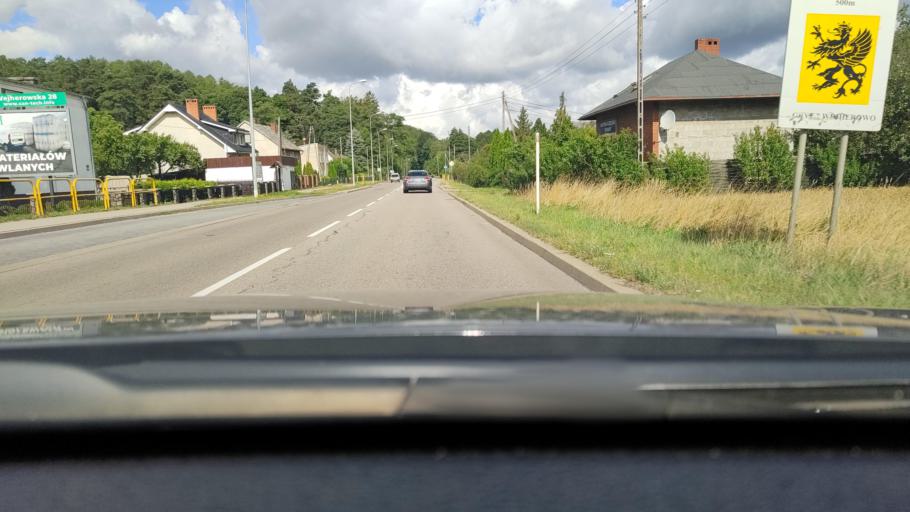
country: PL
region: Pomeranian Voivodeship
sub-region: Powiat wejherowski
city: Wejherowo
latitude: 54.5896
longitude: 18.2440
